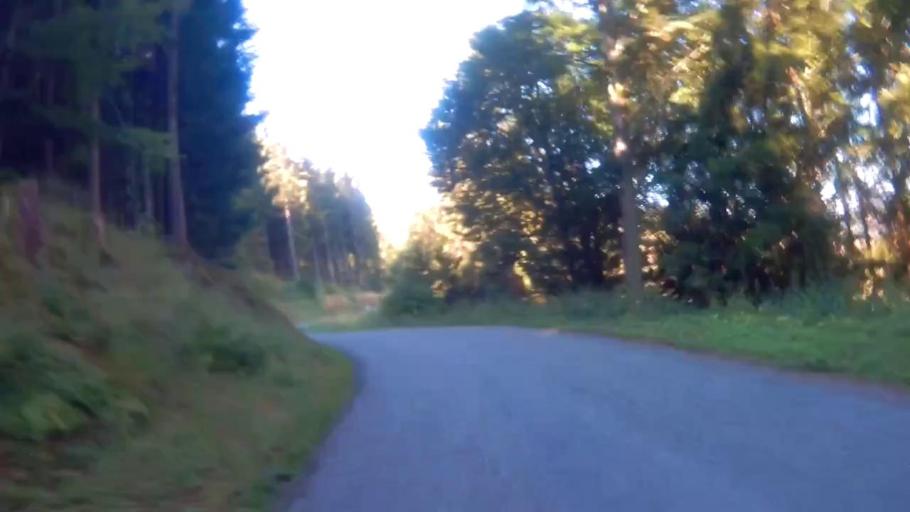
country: DE
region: Baden-Wuerttemberg
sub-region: Freiburg Region
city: Tunau
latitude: 47.7510
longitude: 7.9192
